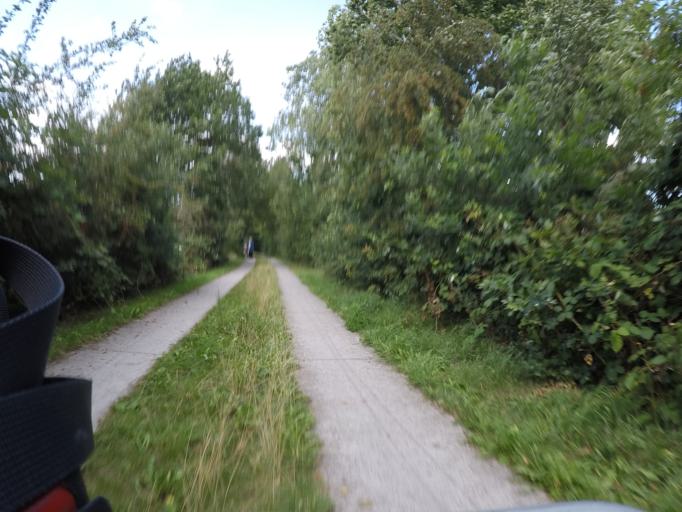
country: DE
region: Lower Saxony
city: Stelle
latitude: 53.4403
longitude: 10.1359
